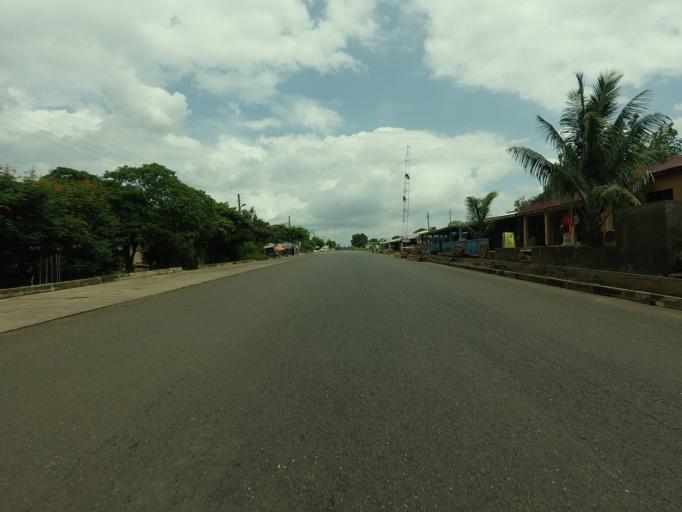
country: GH
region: Volta
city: Ho
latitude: 6.5326
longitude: 0.2289
